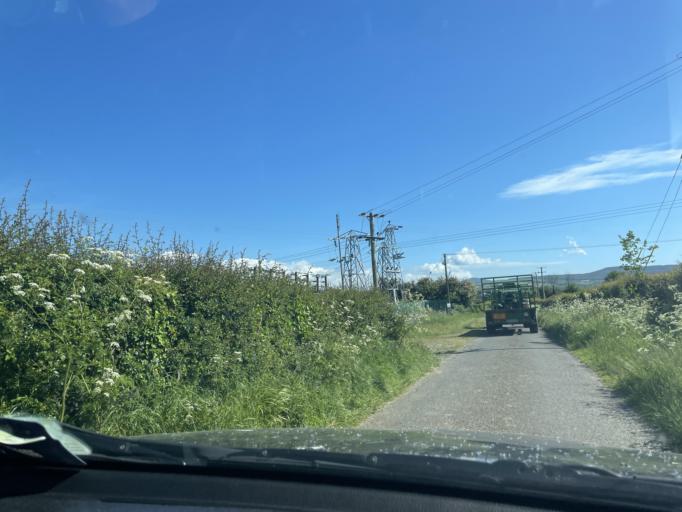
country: IE
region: Leinster
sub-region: County Carlow
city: Bagenalstown
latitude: 52.6349
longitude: -7.0157
